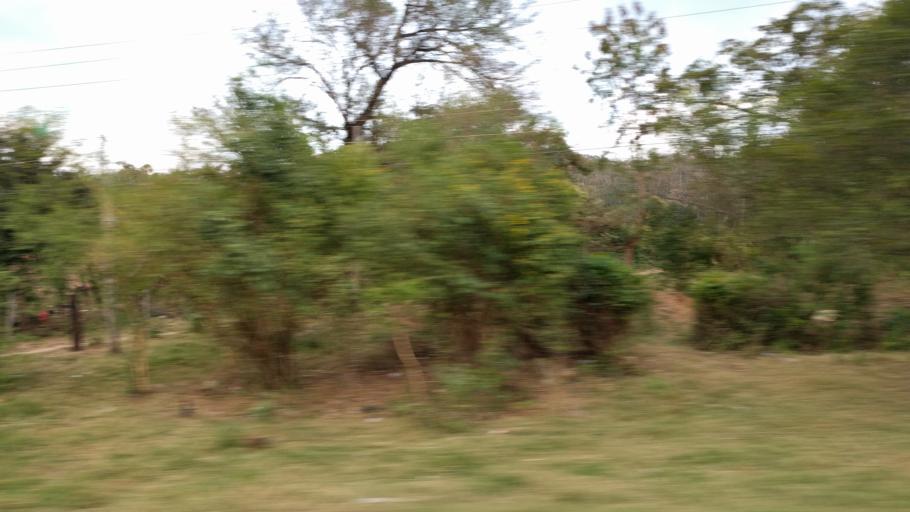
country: BO
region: Santa Cruz
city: Jorochito
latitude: -18.0941
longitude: -63.4504
